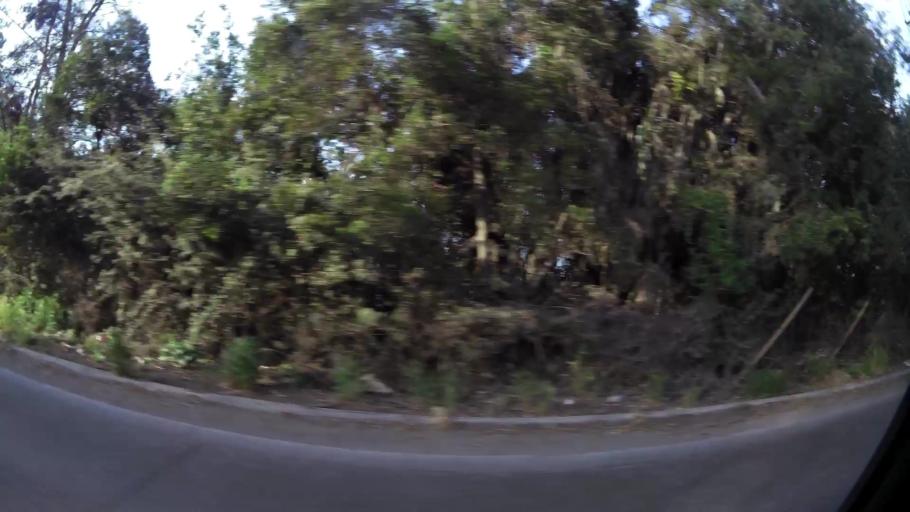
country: CL
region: Santiago Metropolitan
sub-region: Provincia de Maipo
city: San Bernardo
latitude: -33.5609
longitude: -70.7650
